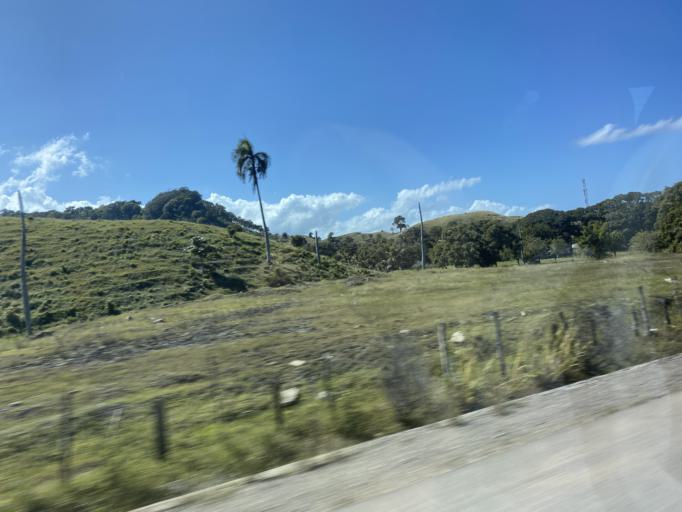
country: DO
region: Puerto Plata
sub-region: Puerto Plata
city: Puerto Plata
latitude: 19.8291
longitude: -70.7618
